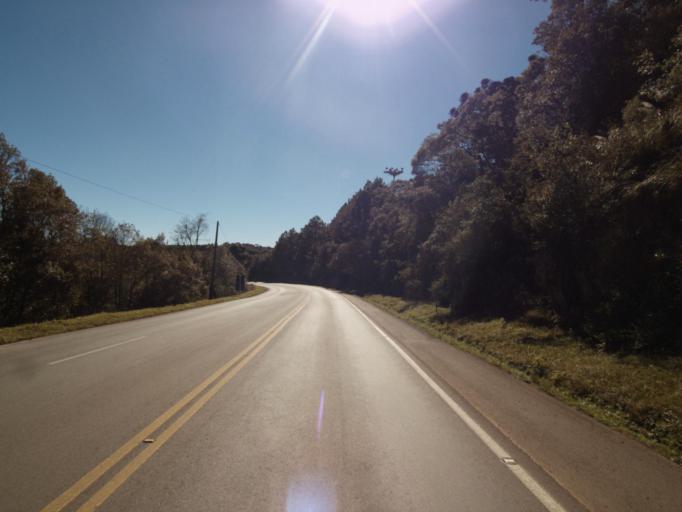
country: BR
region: Santa Catarina
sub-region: Concordia
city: Concordia
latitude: -26.9106
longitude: -51.9047
